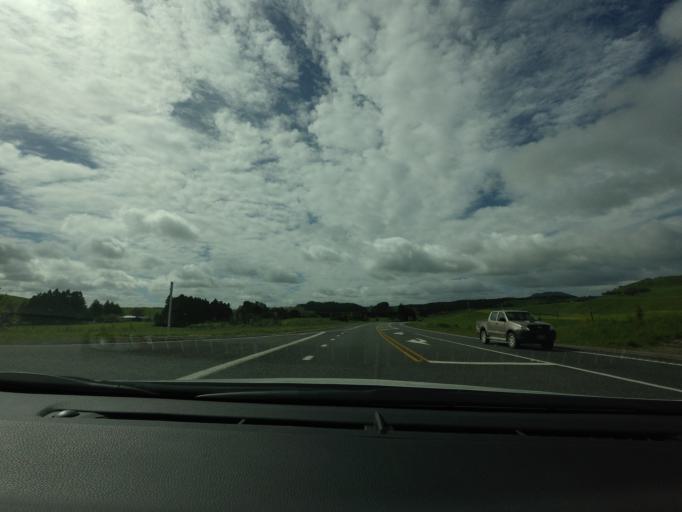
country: NZ
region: Bay of Plenty
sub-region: Rotorua District
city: Rotorua
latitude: -38.2678
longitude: 176.3313
